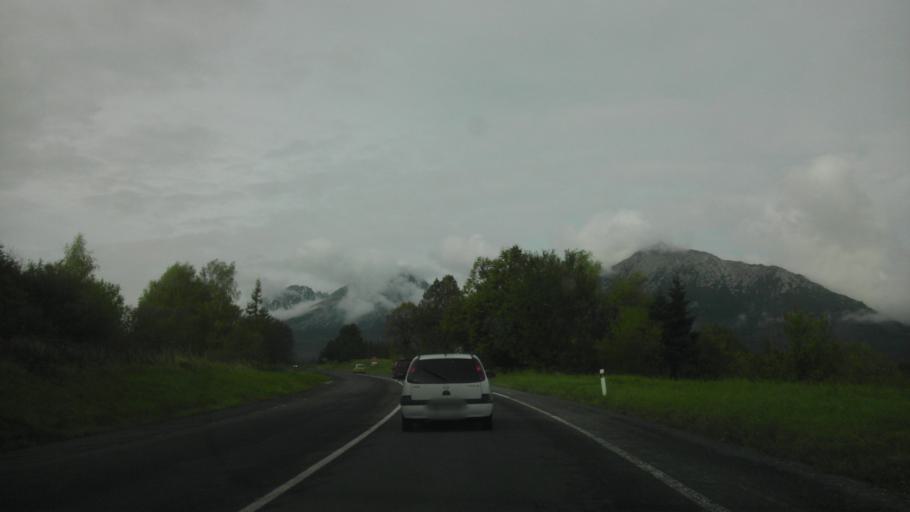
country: SK
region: Presovsky
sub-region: Okres Poprad
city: Nova Lesna
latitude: 49.1156
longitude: 20.2614
